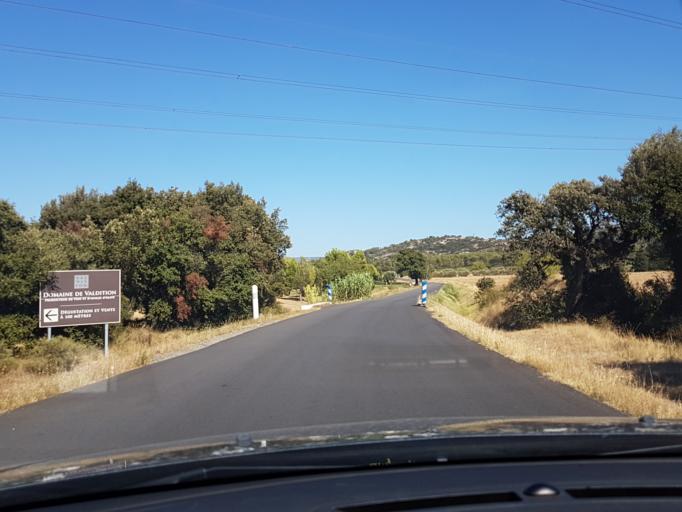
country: FR
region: Provence-Alpes-Cote d'Azur
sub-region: Departement des Bouches-du-Rhone
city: Eygalieres
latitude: 43.7724
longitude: 4.9902
